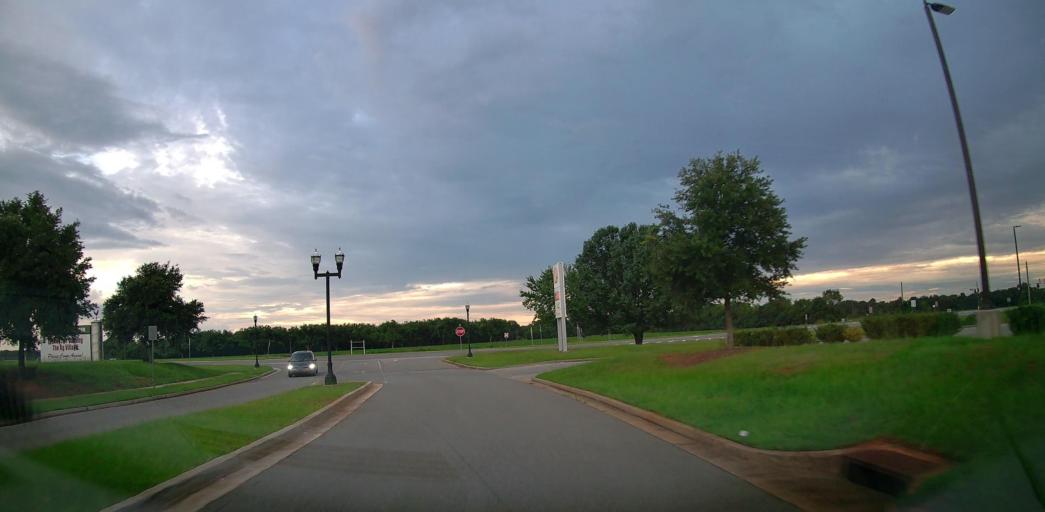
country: US
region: Georgia
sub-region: Houston County
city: Perry
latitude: 32.4338
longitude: -83.7599
